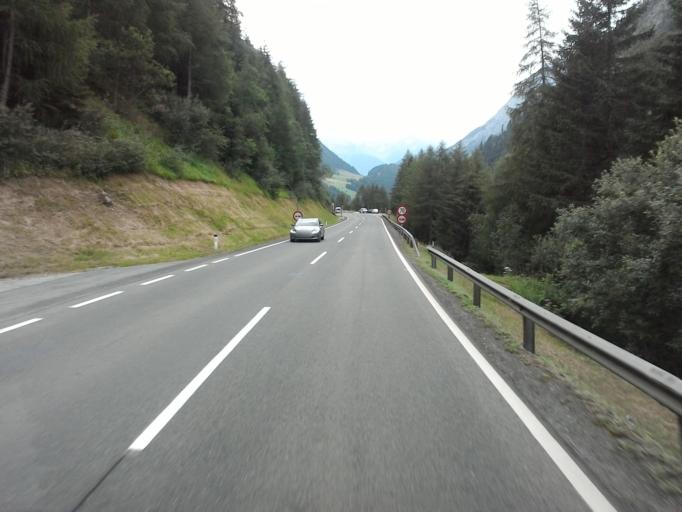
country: AT
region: Tyrol
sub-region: Politischer Bezirk Lienz
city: Matrei in Osttirol
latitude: 47.0799
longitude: 12.5311
